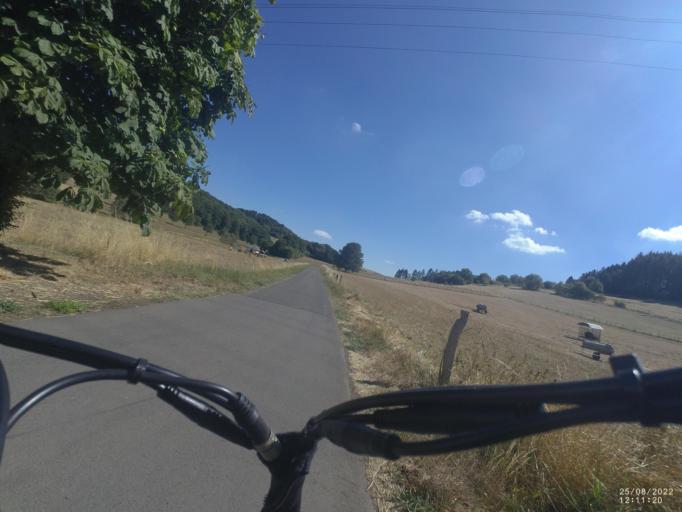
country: DE
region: Rheinland-Pfalz
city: Berlingen
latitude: 50.2378
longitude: 6.7234
